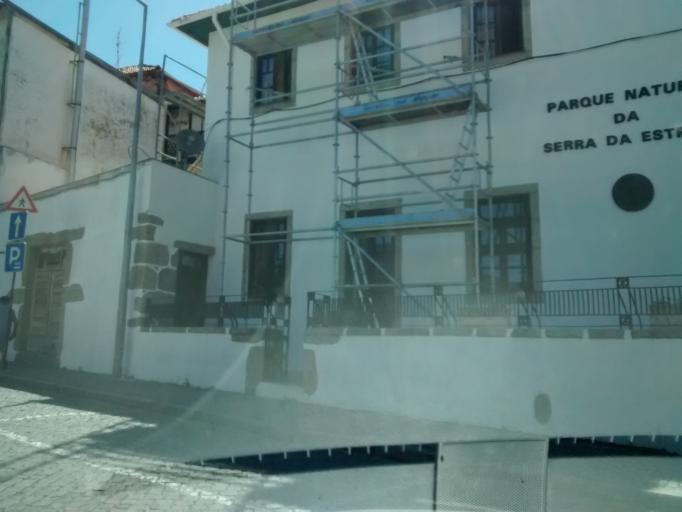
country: PT
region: Guarda
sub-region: Manteigas
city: Manteigas
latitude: 40.4025
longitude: -7.5374
